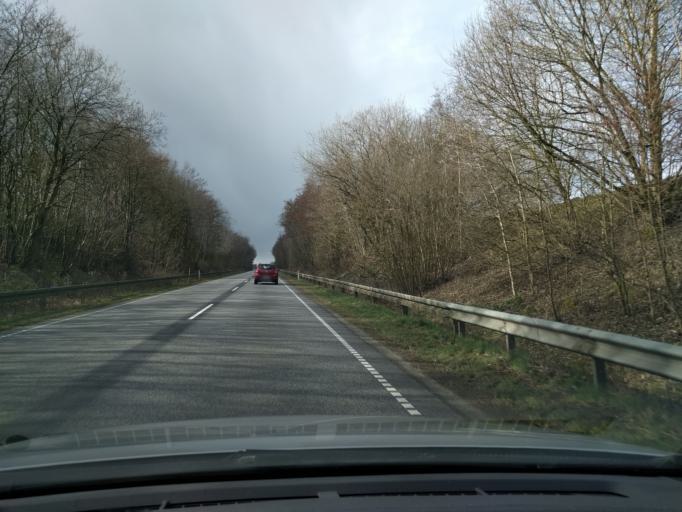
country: DK
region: South Denmark
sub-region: Kolding Kommune
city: Vamdrup
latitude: 55.4353
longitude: 9.2928
